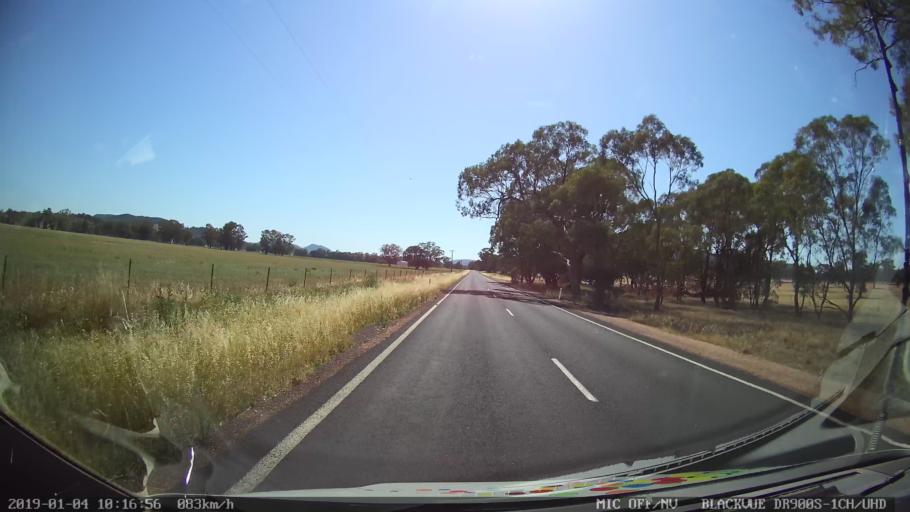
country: AU
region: New South Wales
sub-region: Cabonne
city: Canowindra
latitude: -33.3847
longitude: 148.4441
